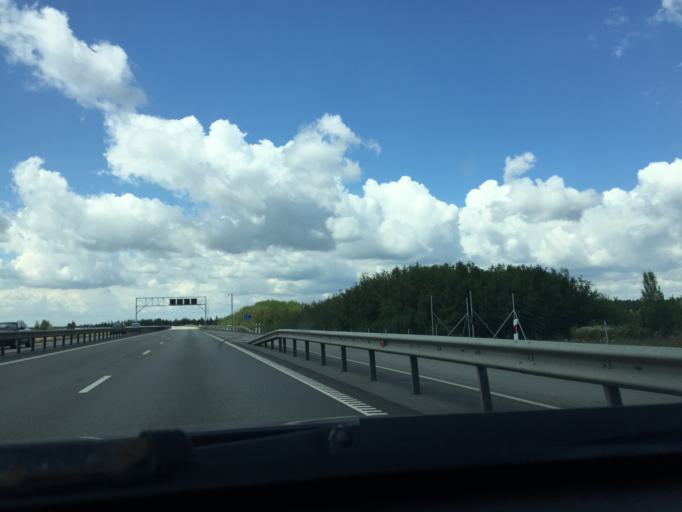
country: LT
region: Panevezys
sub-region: Panevezys City
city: Panevezys
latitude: 55.8036
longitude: 24.3495
